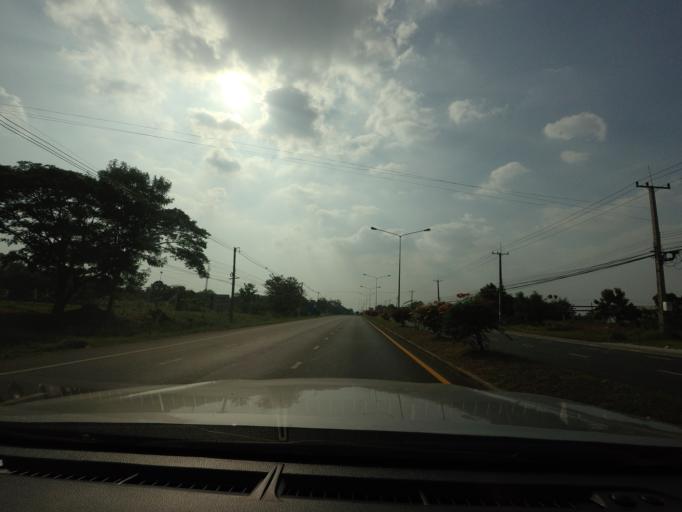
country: TH
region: Sukhothai
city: Sukhothai
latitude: 17.0213
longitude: 99.8656
